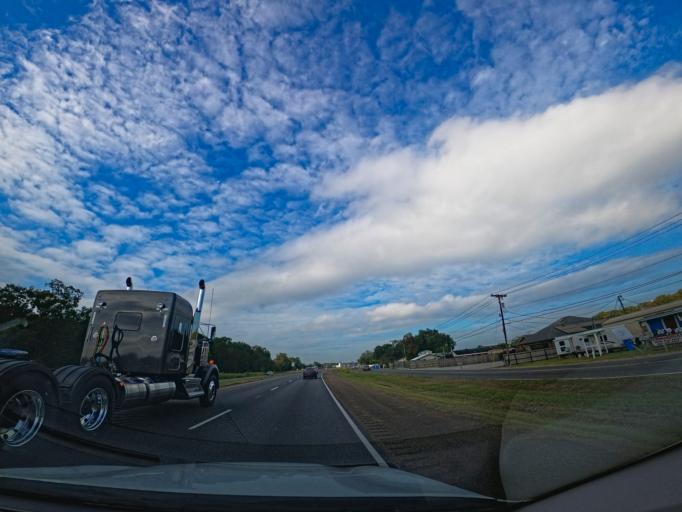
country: US
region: Louisiana
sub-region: Saint Mary Parish
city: Bayou Vista
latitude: 29.6778
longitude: -91.2867
